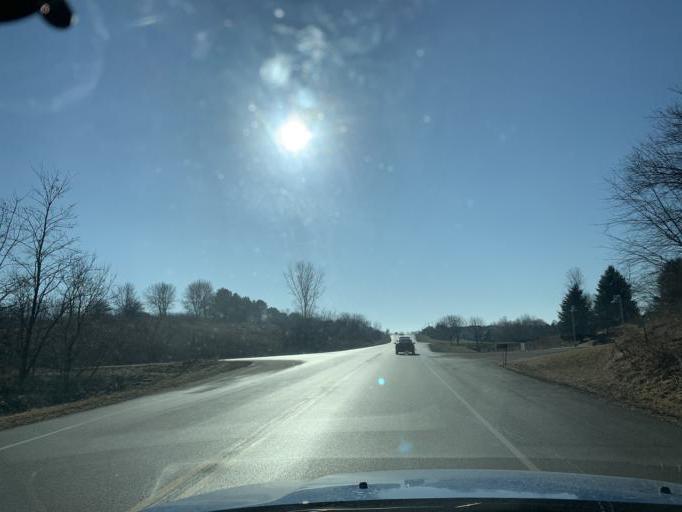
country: US
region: Wisconsin
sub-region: Dane County
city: Verona
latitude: 42.9873
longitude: -89.5139
